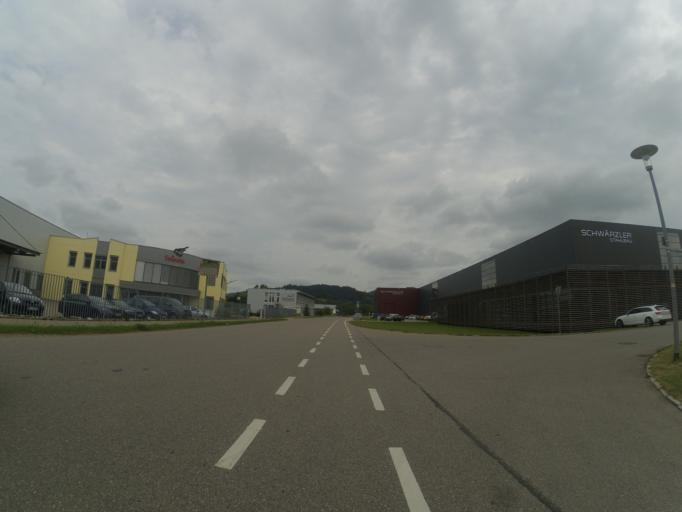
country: DE
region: Baden-Wuerttemberg
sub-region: Tuebingen Region
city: Isny im Allgau
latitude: 47.7056
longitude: 10.0562
